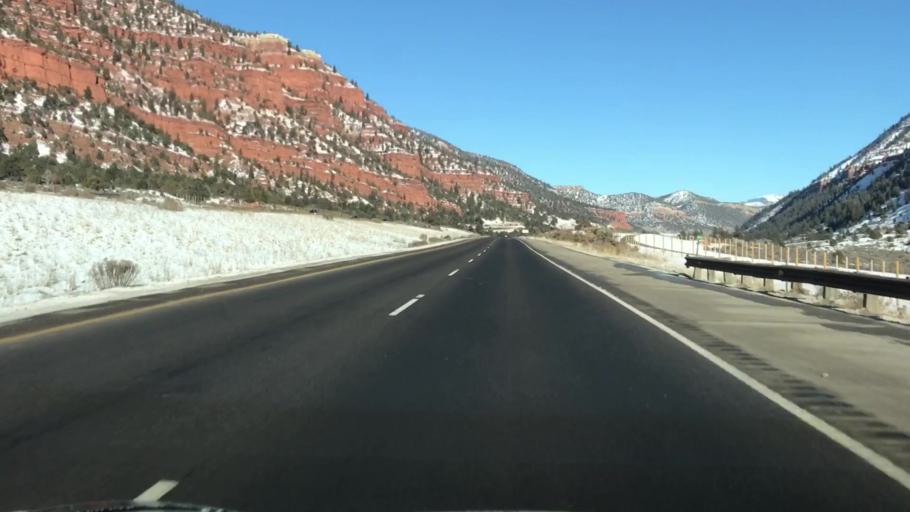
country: US
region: Colorado
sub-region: Eagle County
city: Eagle
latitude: 39.6890
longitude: -106.7506
